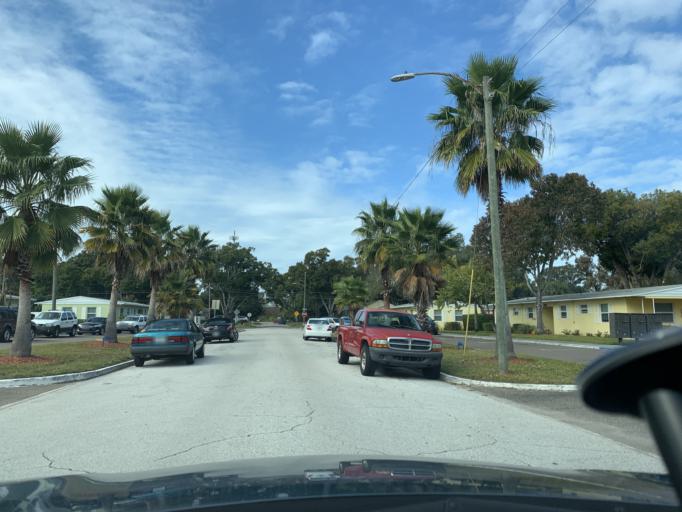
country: US
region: Florida
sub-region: Pinellas County
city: Saint Petersburg
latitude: 27.7893
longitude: -82.6581
